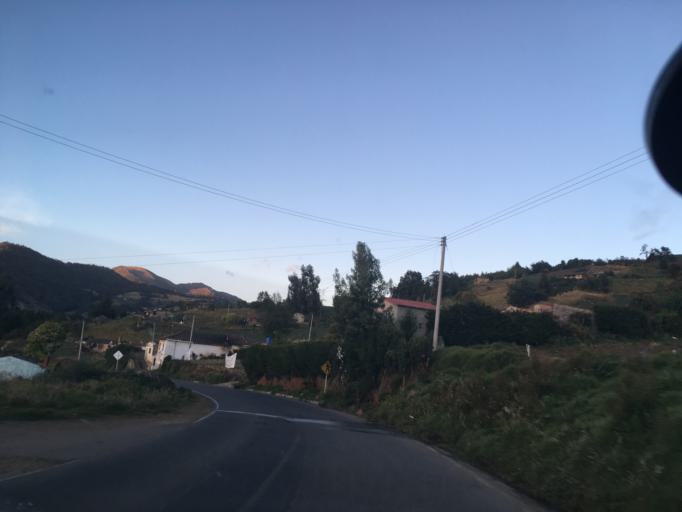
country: CO
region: Boyaca
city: Aquitania
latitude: 5.5793
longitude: -72.8927
